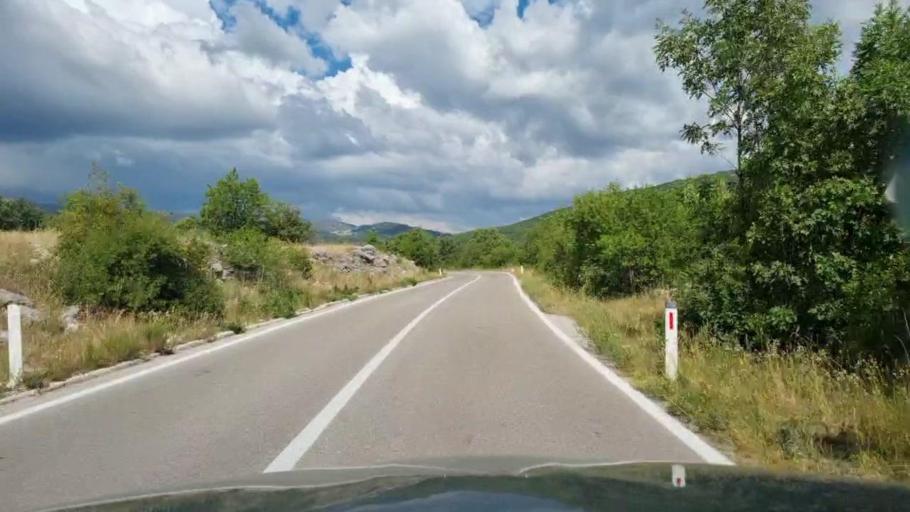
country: BA
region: Federation of Bosnia and Herzegovina
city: Blagaj
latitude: 43.2563
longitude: 17.9975
